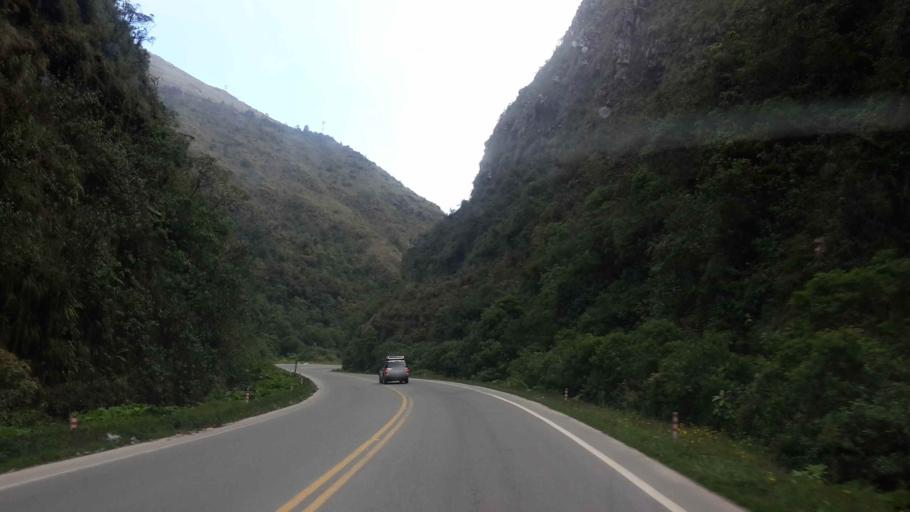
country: BO
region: Cochabamba
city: Colomi
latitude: -17.2095
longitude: -65.8887
